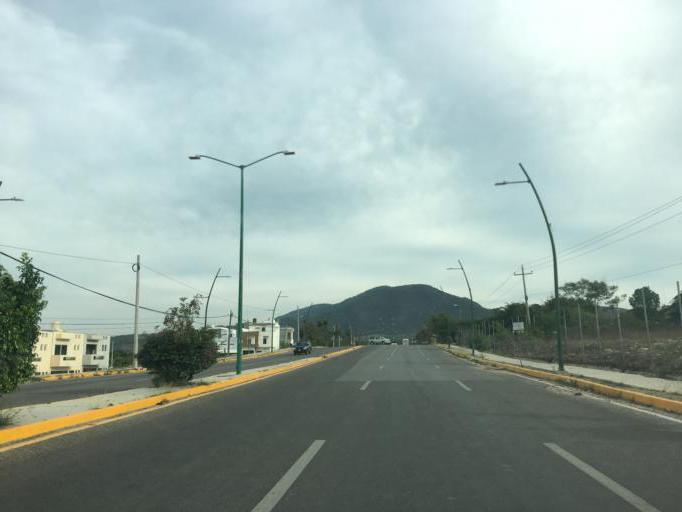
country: MX
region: Chiapas
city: Tuxtla Gutierrez
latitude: 16.7694
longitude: -93.1716
